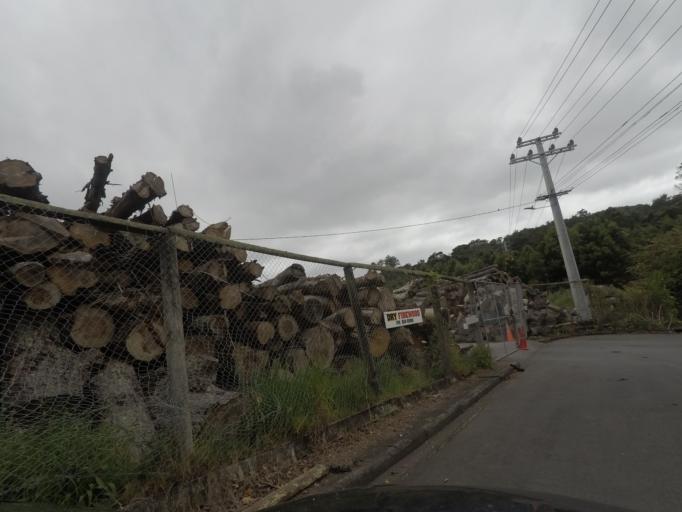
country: NZ
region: Auckland
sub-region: Auckland
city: Waitakere
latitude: -36.9058
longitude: 174.6378
